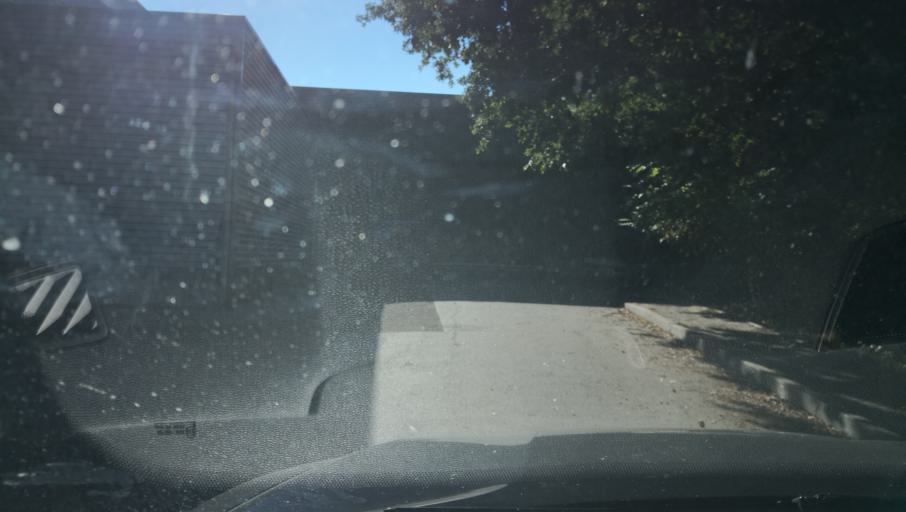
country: PT
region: Vila Real
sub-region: Vila Real
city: Vila Real
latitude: 41.2898
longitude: -7.7393
